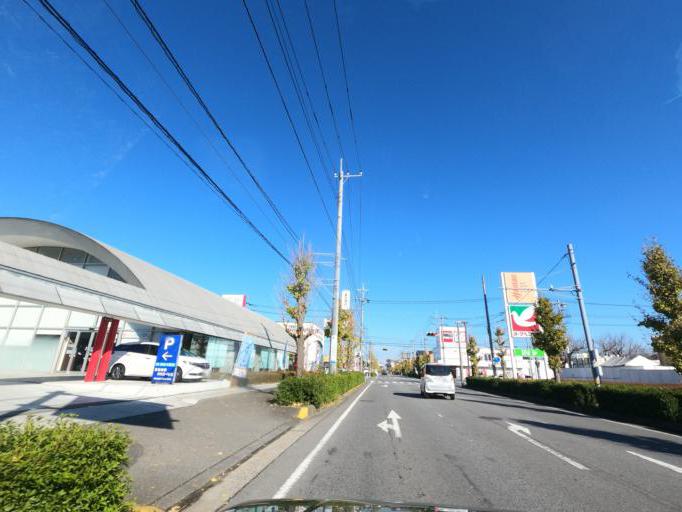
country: JP
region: Ibaraki
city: Mitsukaido
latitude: 35.9764
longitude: 139.9727
